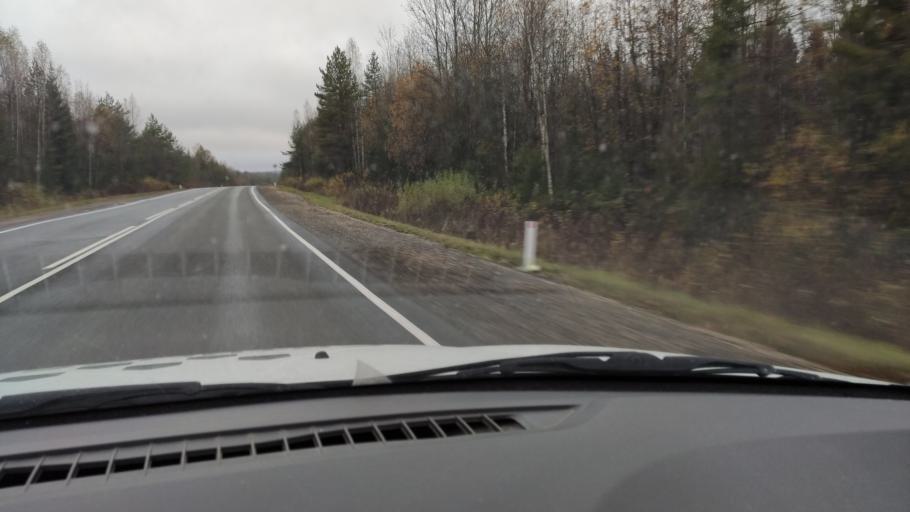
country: RU
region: Kirov
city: Omutninsk
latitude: 58.7023
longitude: 52.1111
